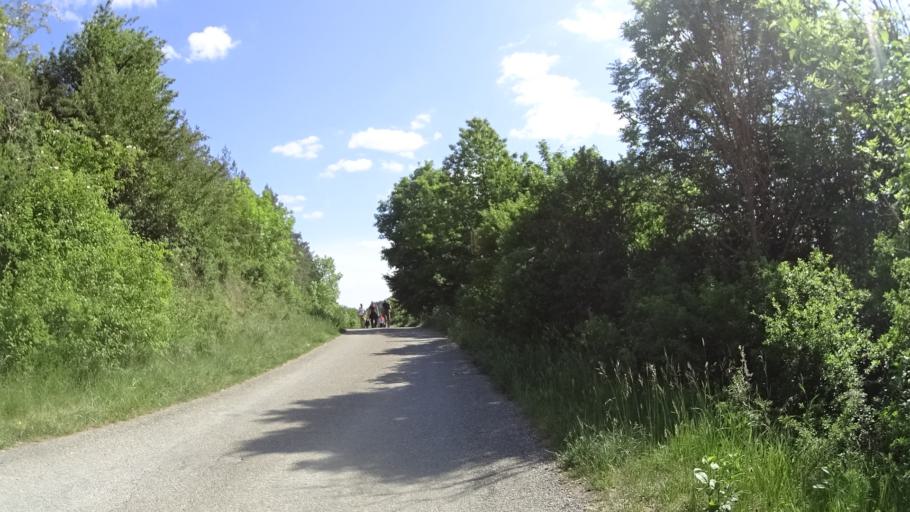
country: DE
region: Baden-Wuerttemberg
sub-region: Karlsruhe Region
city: Hardheim
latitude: 49.5866
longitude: 9.4855
